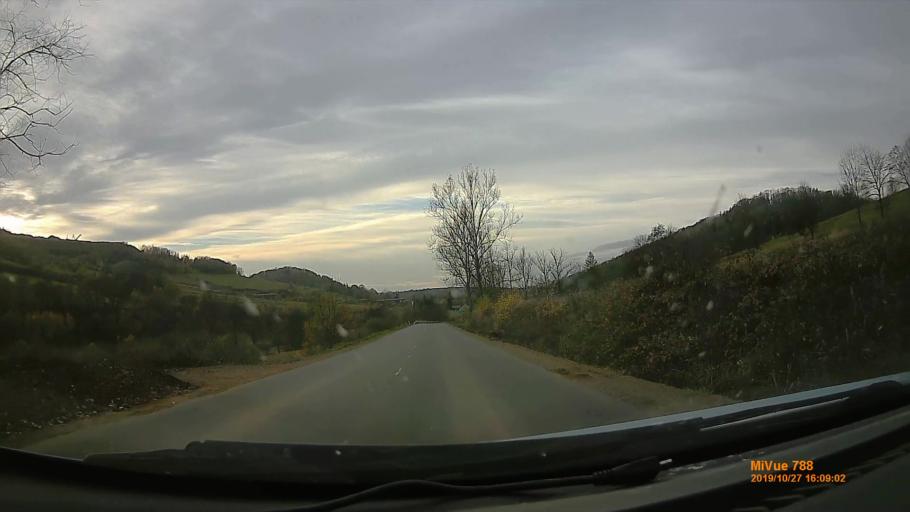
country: PL
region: Lower Silesian Voivodeship
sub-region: Powiat klodzki
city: Nowa Ruda
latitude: 50.5498
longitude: 16.4522
